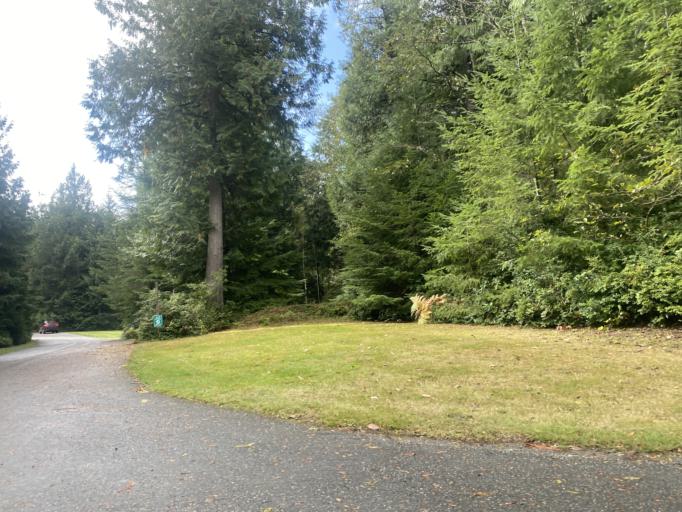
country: US
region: Washington
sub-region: Island County
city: Langley
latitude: 48.0095
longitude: -122.4047
